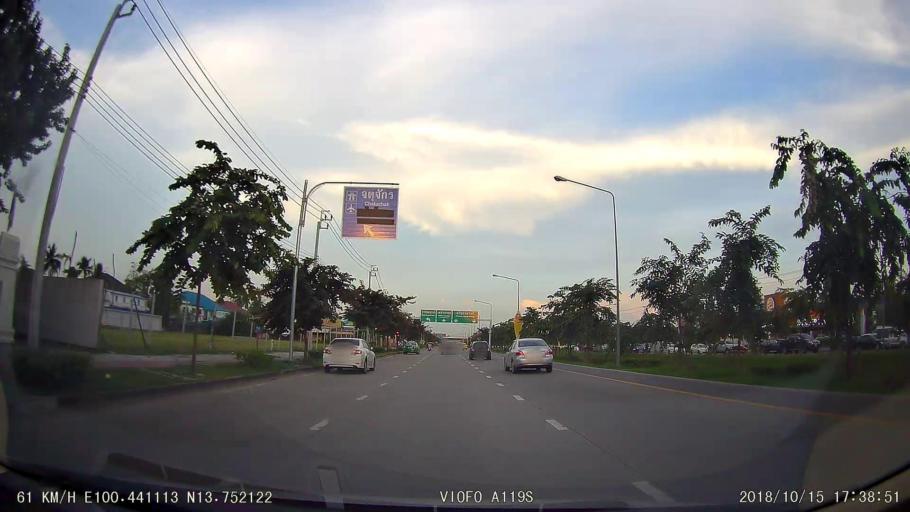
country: TH
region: Bangkok
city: Taling Chan
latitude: 13.7521
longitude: 100.4414
